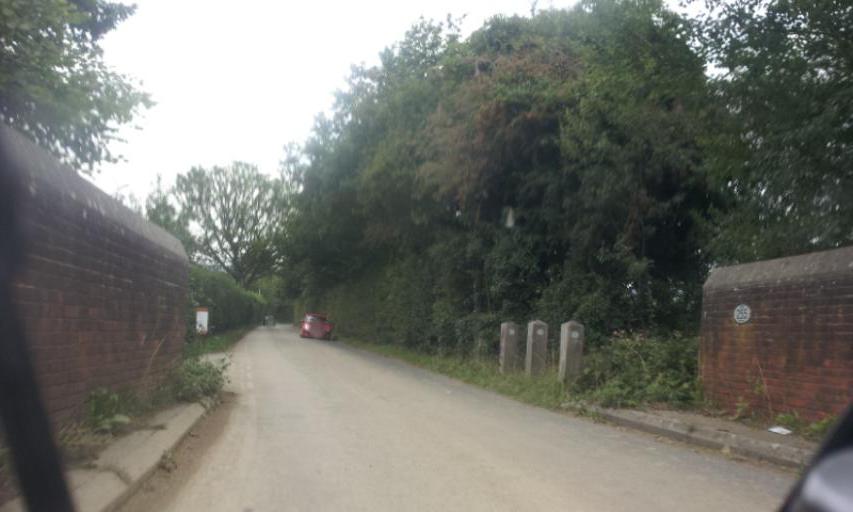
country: GB
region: England
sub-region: Kent
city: Tonbridge
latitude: 51.1872
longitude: 0.3176
